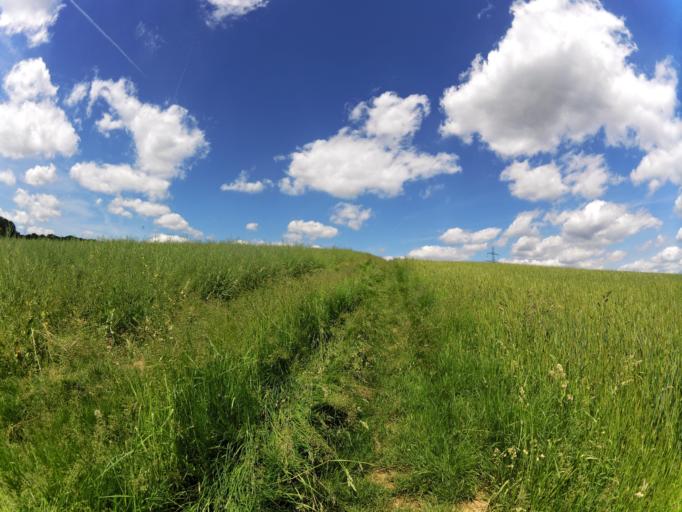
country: DE
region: Bavaria
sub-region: Regierungsbezirk Unterfranken
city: Waldbrunn
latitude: 49.7750
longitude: 9.7692
